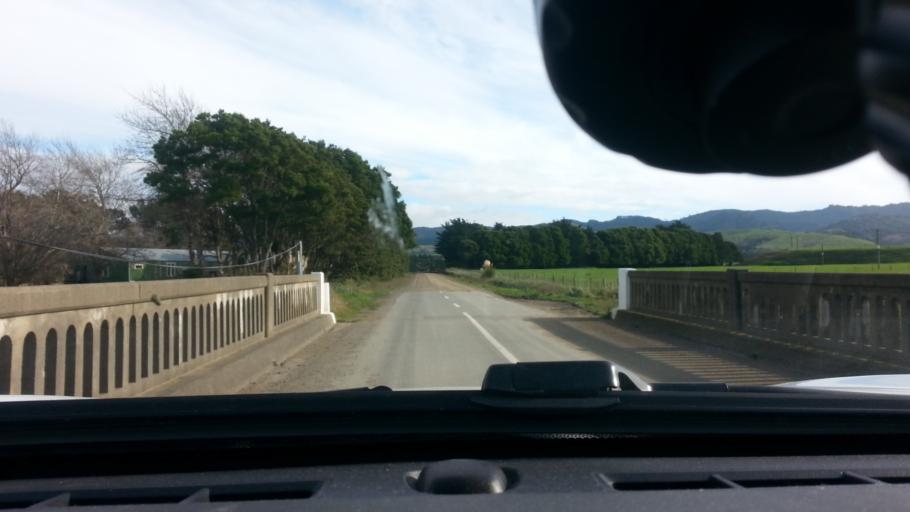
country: NZ
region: Wellington
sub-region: Masterton District
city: Castlepoint
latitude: -41.1278
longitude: 176.0308
